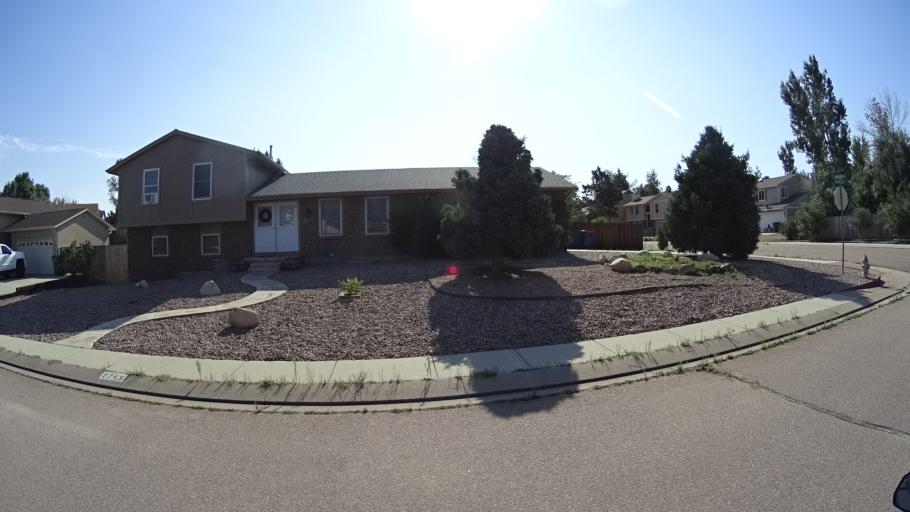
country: US
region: Colorado
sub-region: El Paso County
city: Black Forest
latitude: 38.9451
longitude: -104.7722
